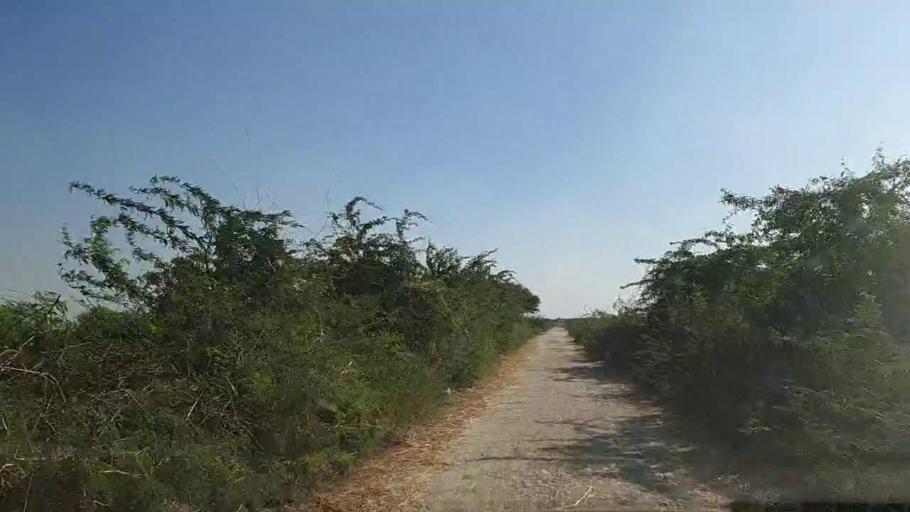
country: PK
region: Sindh
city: Daro Mehar
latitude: 24.7540
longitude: 68.0627
